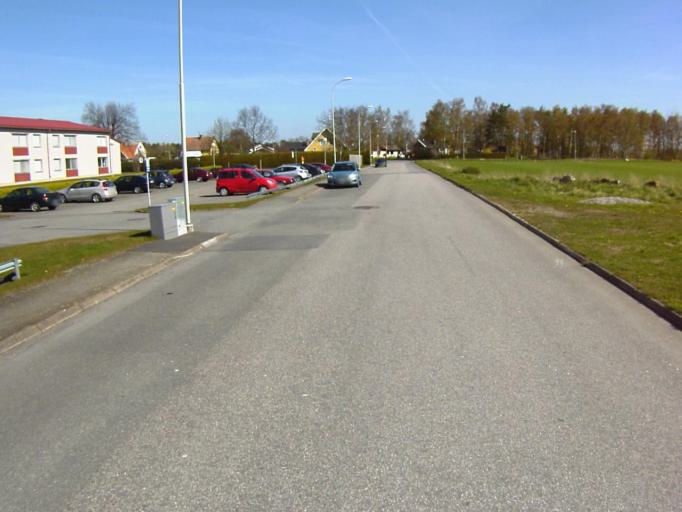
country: SE
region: Skane
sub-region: Kristianstads Kommun
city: Norra Asum
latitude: 55.9991
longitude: 14.0935
